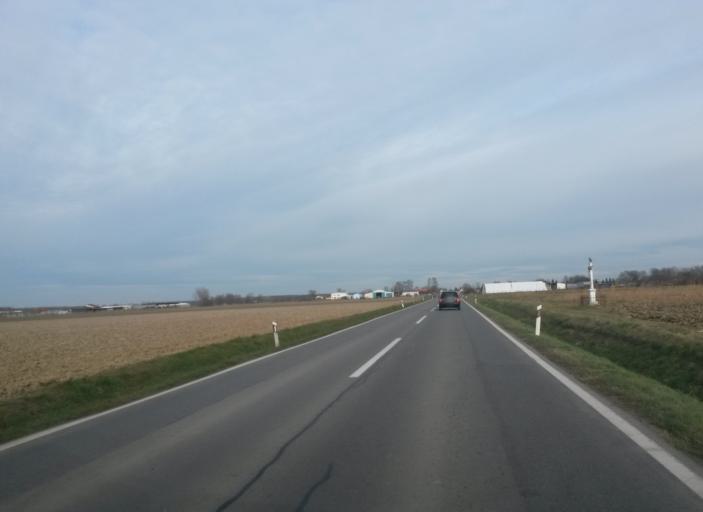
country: HR
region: Osjecko-Baranjska
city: Viskovci
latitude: 45.3948
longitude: 18.4569
